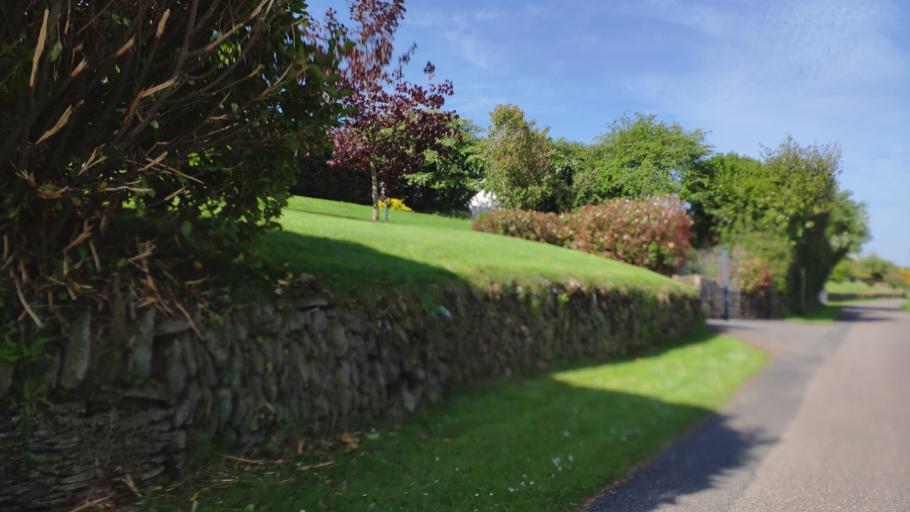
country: IE
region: Munster
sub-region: County Cork
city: Blarney
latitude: 51.9177
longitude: -8.5378
